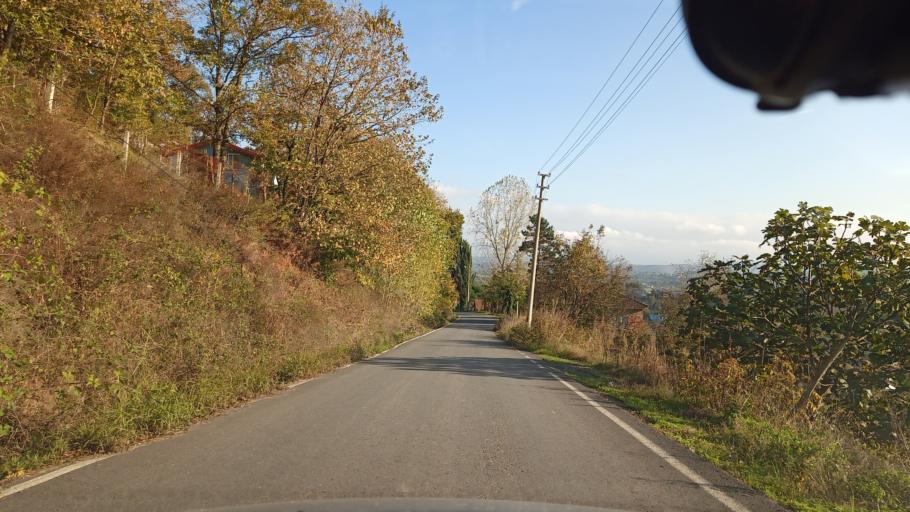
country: TR
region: Sakarya
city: Karasu
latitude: 41.0589
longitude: 30.6236
